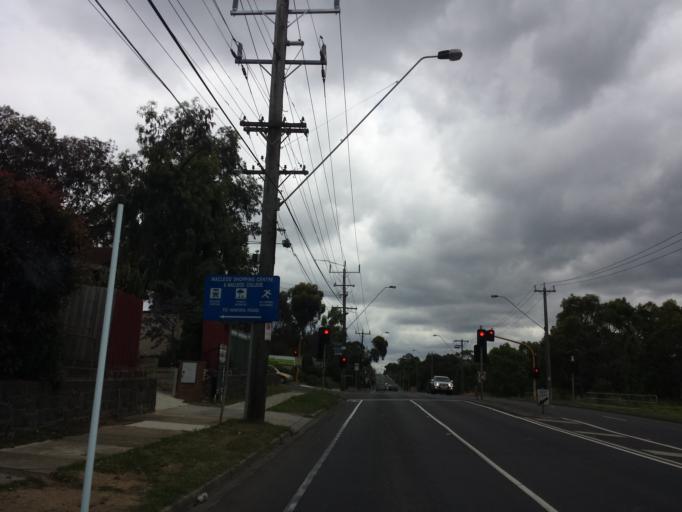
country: AU
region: Victoria
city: Macleod
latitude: -37.7304
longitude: 145.0794
